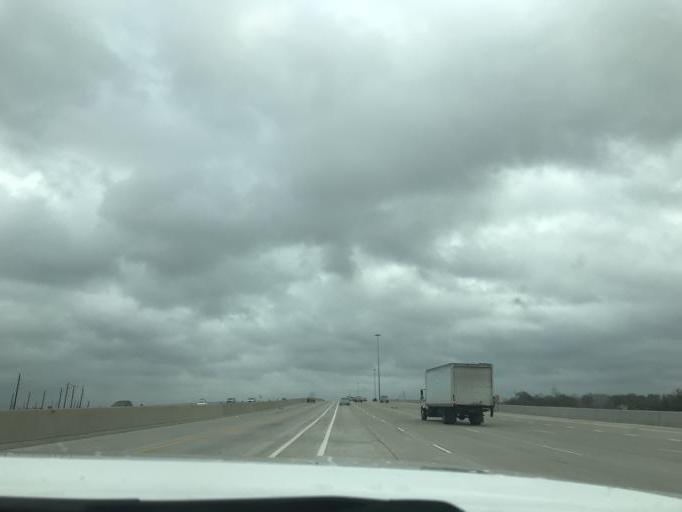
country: US
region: Texas
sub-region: Fort Bend County
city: Greatwood
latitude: 29.5551
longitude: -95.7207
